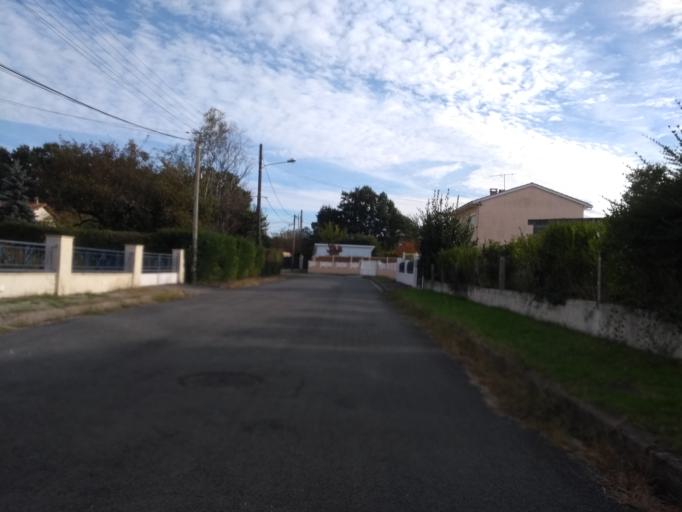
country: FR
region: Aquitaine
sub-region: Departement de la Gironde
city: Pessac
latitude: 44.7884
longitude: -0.6710
